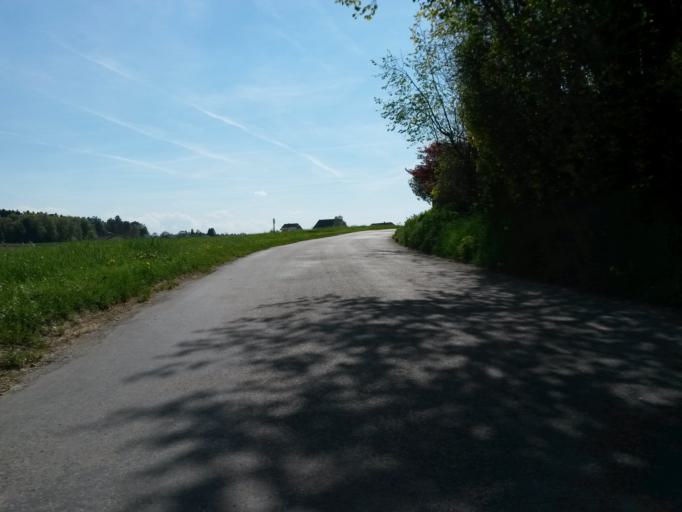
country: CH
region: Bern
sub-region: Oberaargau
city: Herzogenbuchsee
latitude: 47.2016
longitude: 7.7423
